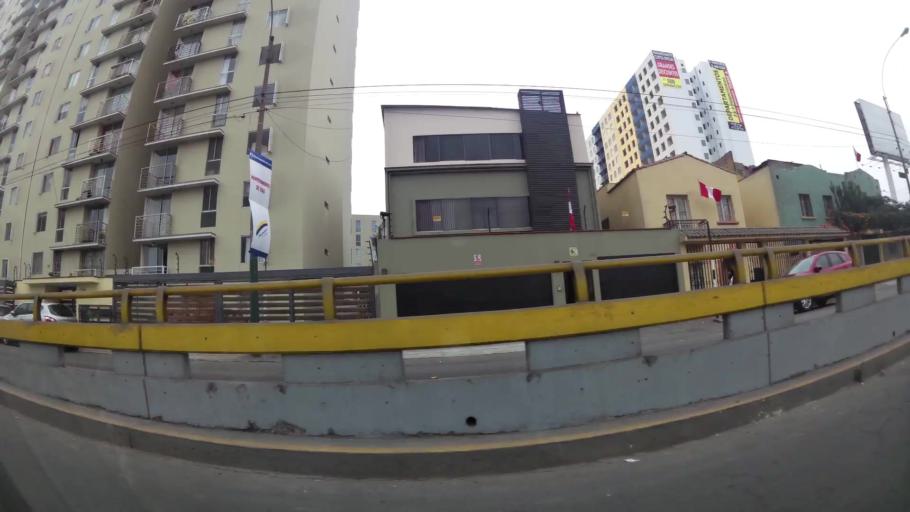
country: PE
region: Lima
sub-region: Lima
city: San Isidro
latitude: -12.0870
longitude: -77.0638
